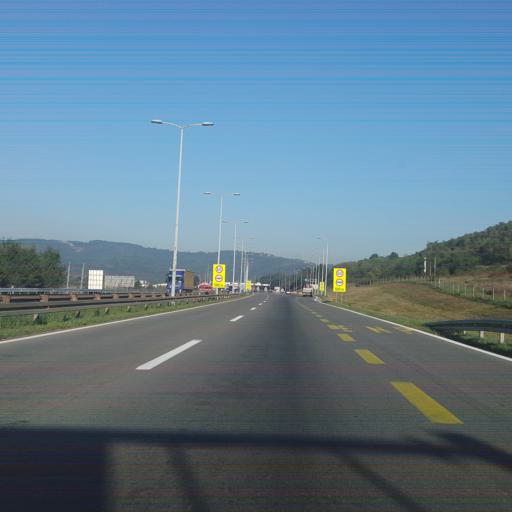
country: RS
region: Central Serbia
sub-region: Belgrade
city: Zvezdara
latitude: 44.7139
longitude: 20.5616
